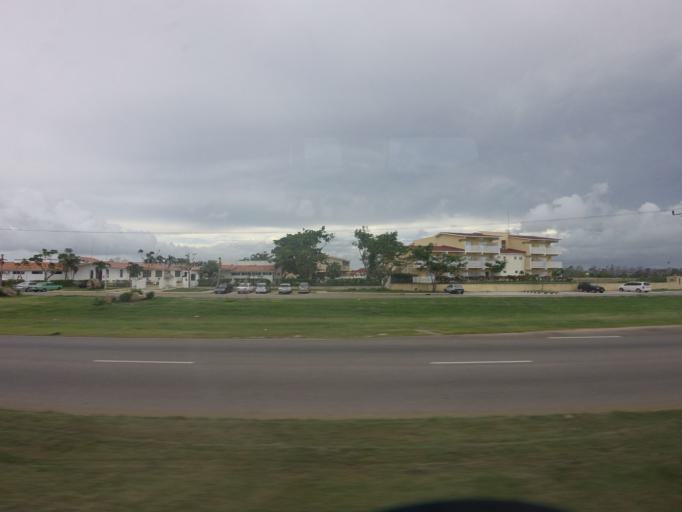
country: CU
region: Matanzas
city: Varadero
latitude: 23.1584
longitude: -81.2344
